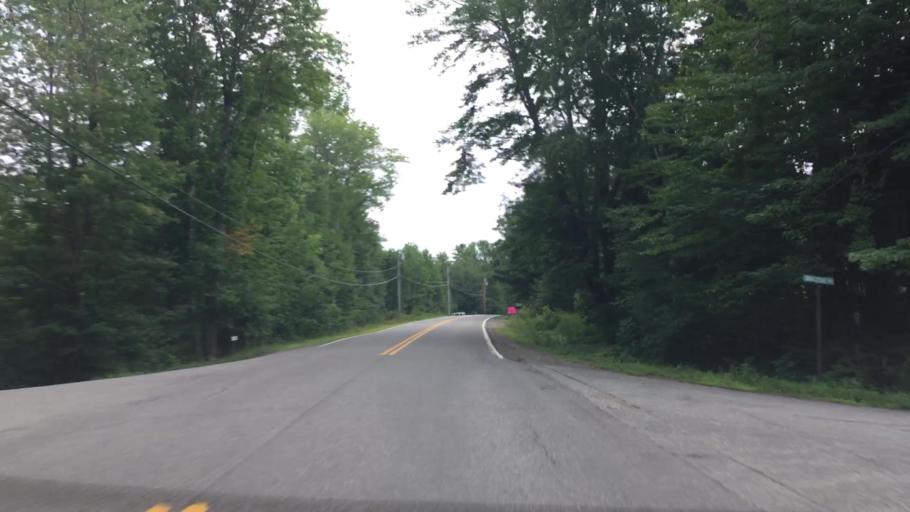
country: US
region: Maine
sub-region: Waldo County
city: Lincolnville
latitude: 44.3385
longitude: -69.0558
